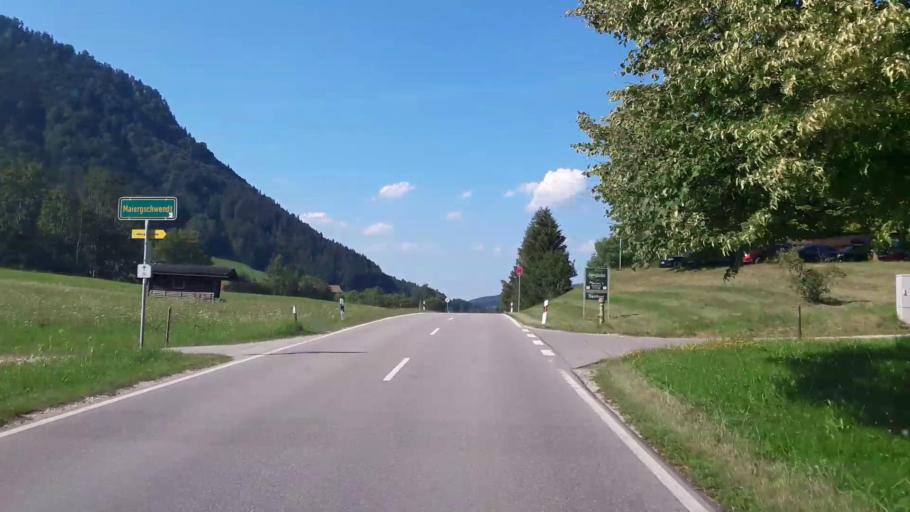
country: DE
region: Bavaria
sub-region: Upper Bavaria
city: Ruhpolding
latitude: 47.7540
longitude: 12.6306
